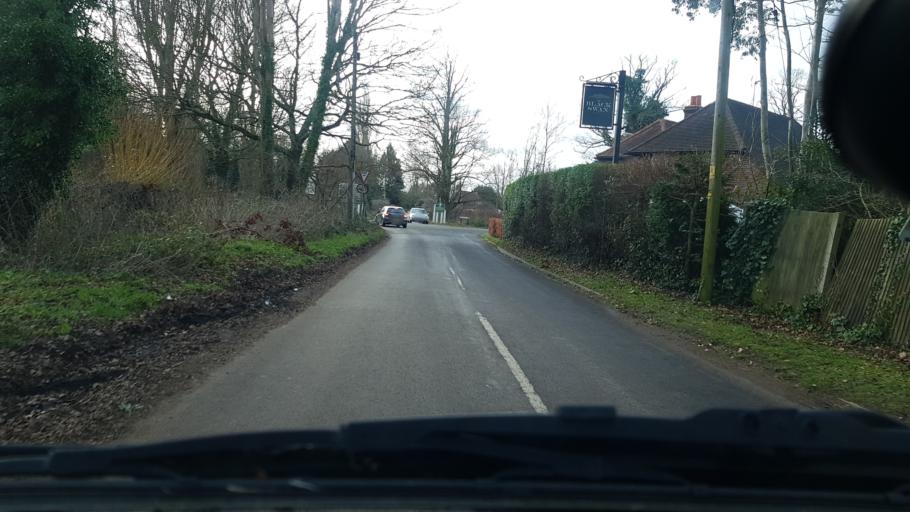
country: GB
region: England
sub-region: Surrey
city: East Horsley
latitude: 51.3046
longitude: -0.4385
